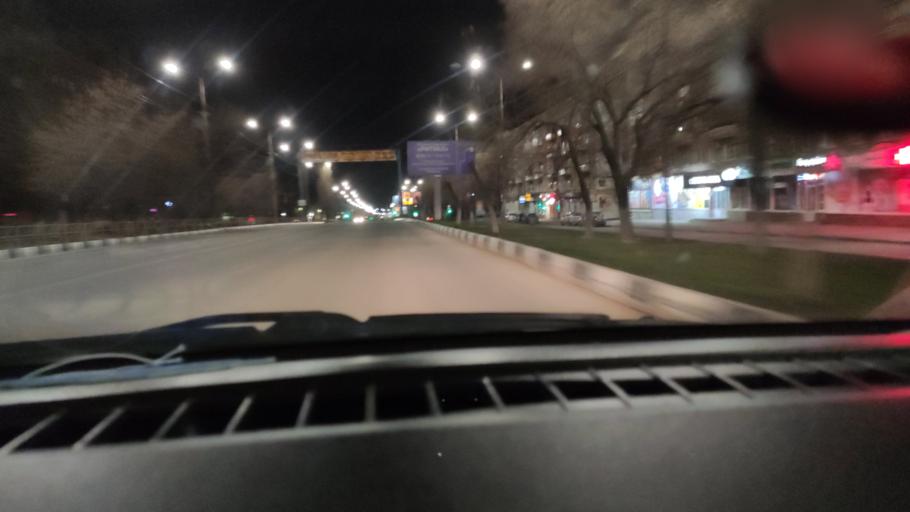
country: RU
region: Saratov
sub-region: Saratovskiy Rayon
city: Saratov
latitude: 51.6014
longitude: 45.9687
